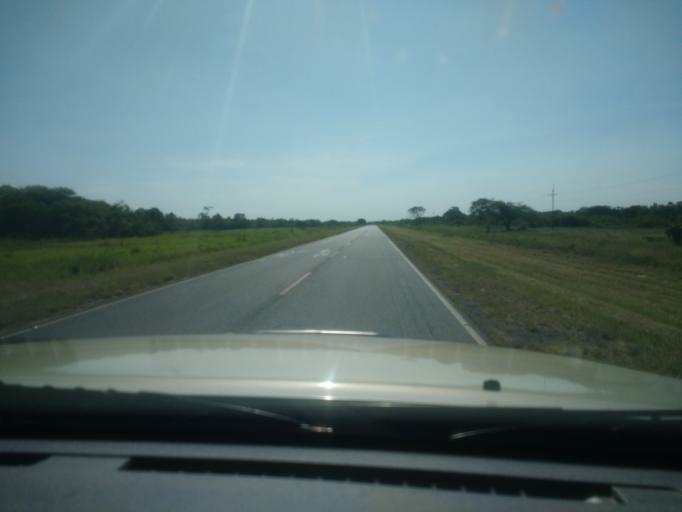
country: PY
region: Presidente Hayes
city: Benjamin Aceval
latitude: -24.9215
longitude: -57.5866
